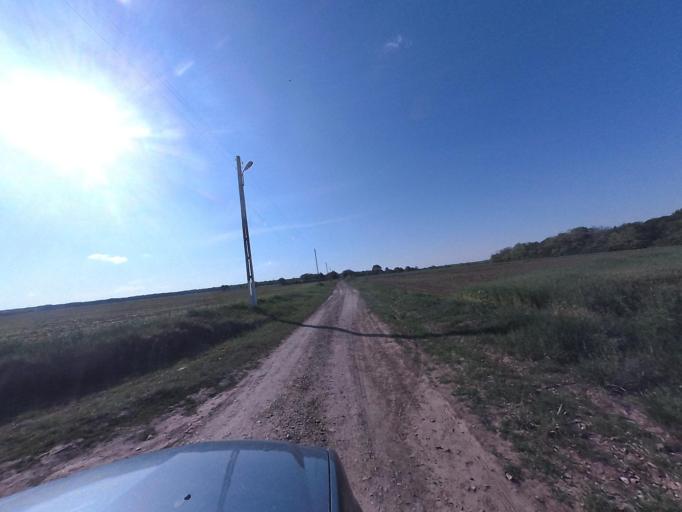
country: RO
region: Neamt
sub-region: Comuna Dulcesti
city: Dulcesti
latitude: 47.0005
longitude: 26.7778
